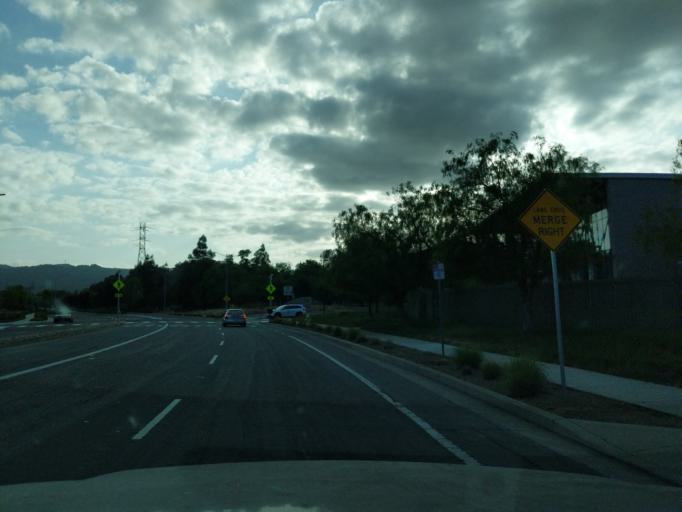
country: US
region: California
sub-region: Santa Clara County
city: Morgan Hill
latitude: 37.1127
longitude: -121.6451
